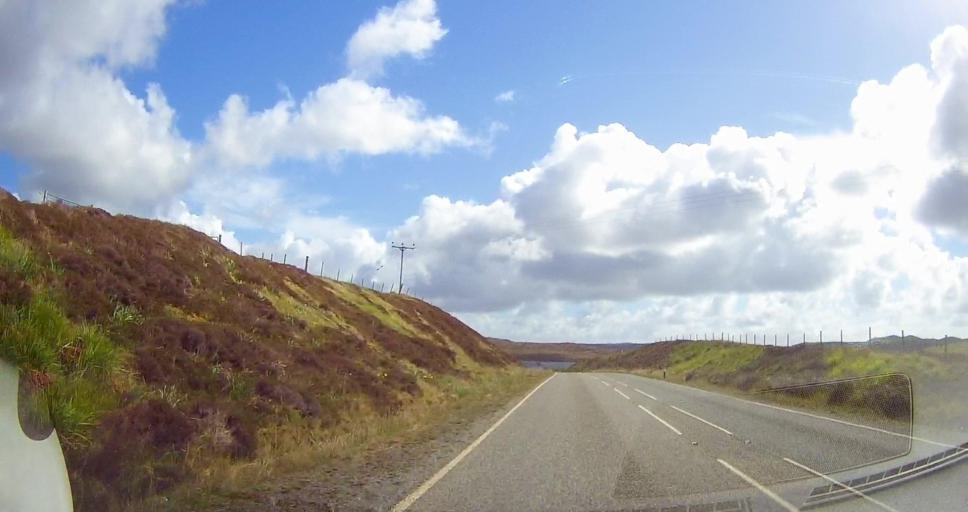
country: GB
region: Scotland
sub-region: Shetland Islands
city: Lerwick
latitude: 60.4700
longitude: -1.4069
